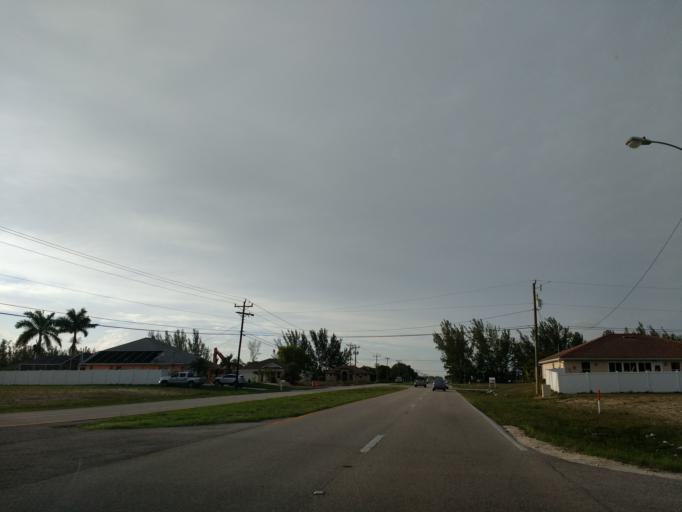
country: US
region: Florida
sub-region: Lee County
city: Cape Coral
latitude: 26.5976
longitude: -82.0069
